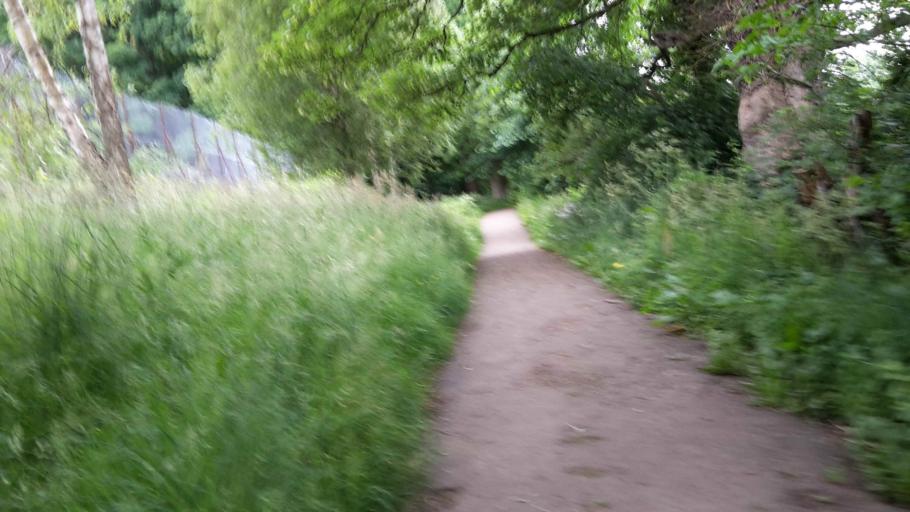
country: GB
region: Scotland
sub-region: South Lanarkshire
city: Uddingston
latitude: 55.8192
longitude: -4.0943
